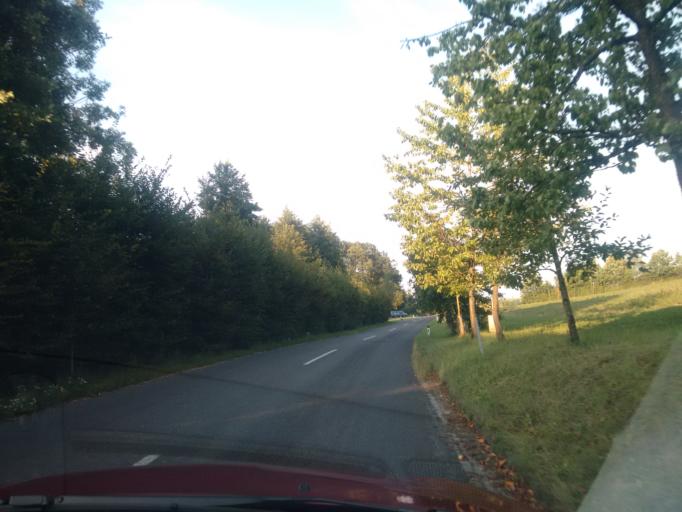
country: AT
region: Upper Austria
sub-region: Wels-Land
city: Bachmanning
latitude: 48.1589
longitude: 13.7737
